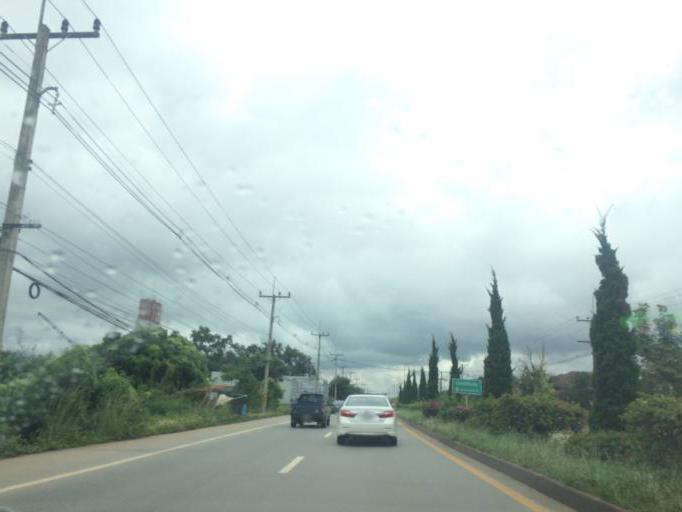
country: TH
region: Chiang Rai
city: Chiang Rai
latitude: 20.0146
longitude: 99.8693
